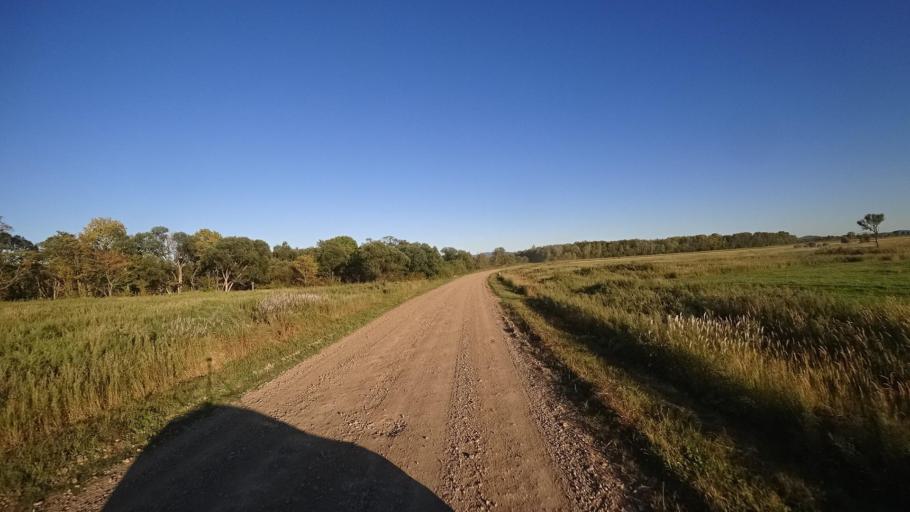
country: RU
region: Primorskiy
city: Kirovskiy
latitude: 44.8229
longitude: 133.6028
